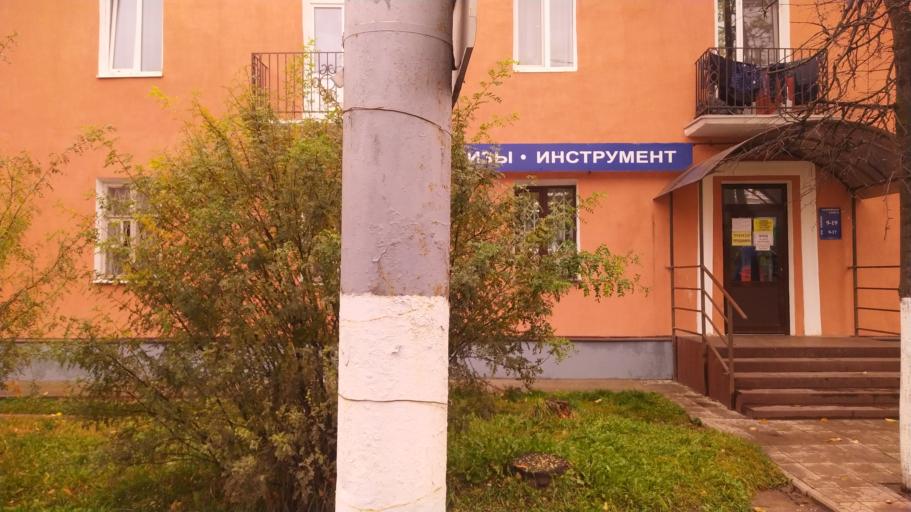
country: RU
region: Tverskaya
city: Tver
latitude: 56.8408
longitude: 35.9339
